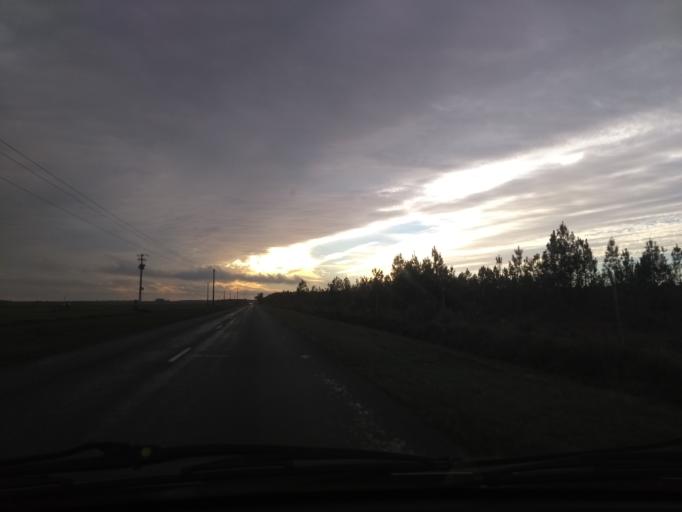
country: FR
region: Aquitaine
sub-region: Departement de la Gironde
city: Saucats
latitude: 44.6285
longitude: -0.6600
